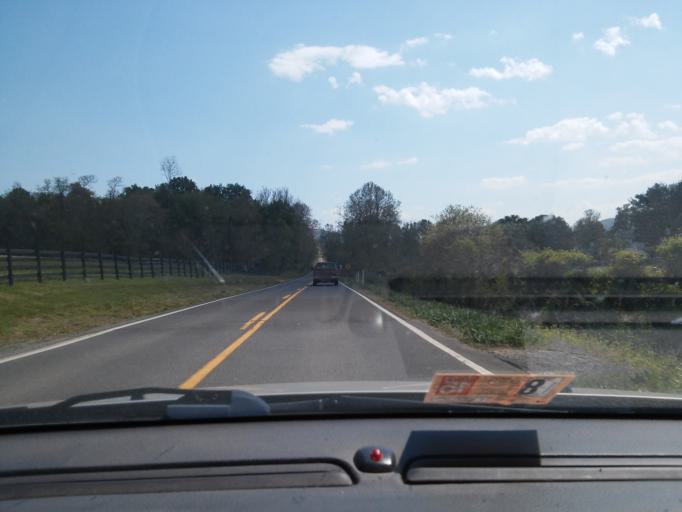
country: US
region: Virginia
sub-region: Rappahannock County
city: Washington
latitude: 38.7813
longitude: -78.1039
